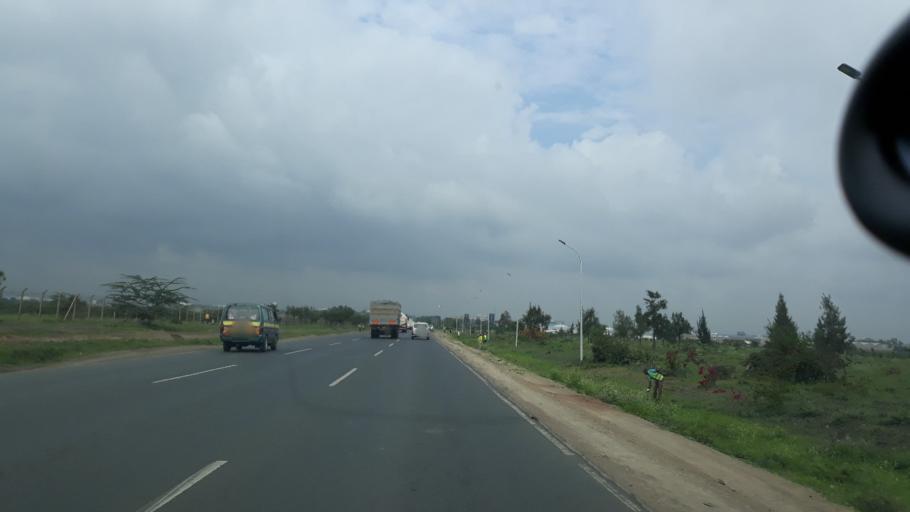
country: KE
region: Nairobi Area
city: Pumwani
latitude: -1.3446
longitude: 36.9006
